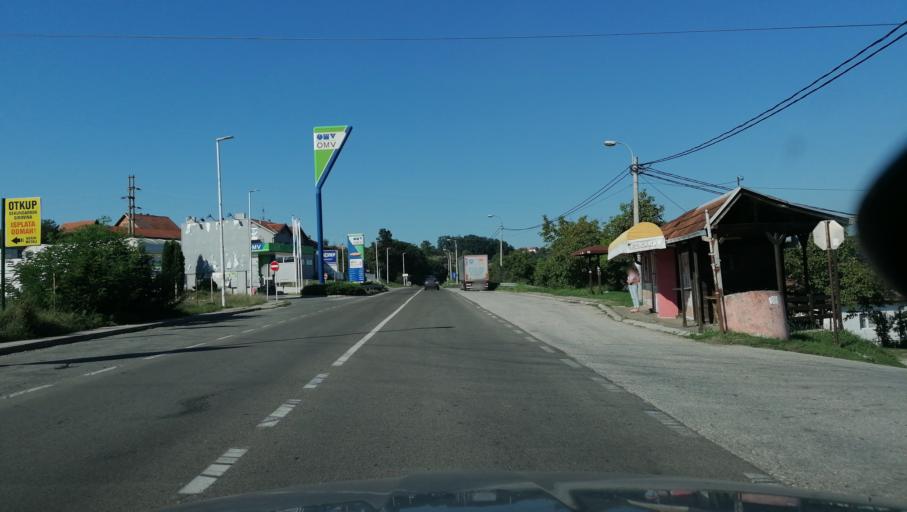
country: RS
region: Central Serbia
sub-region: Raski Okrug
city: Kraljevo
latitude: 43.7111
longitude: 20.6171
